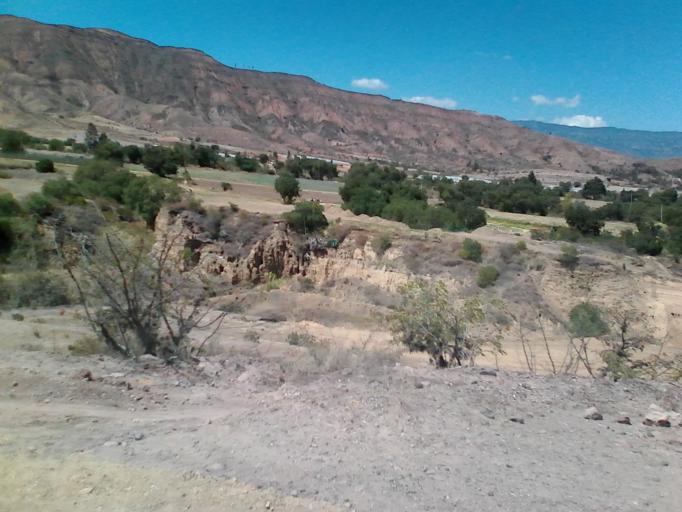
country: CO
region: Boyaca
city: Sachica
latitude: 5.5716
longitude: -73.5410
